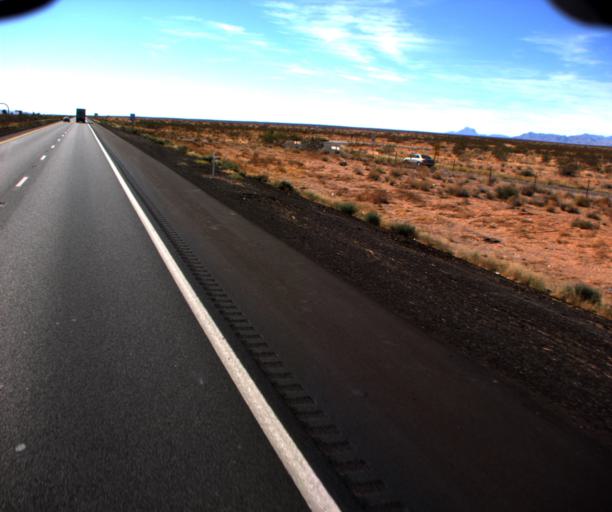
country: US
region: Arizona
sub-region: Mohave County
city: Beaver Dam
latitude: 36.8862
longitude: -113.9388
